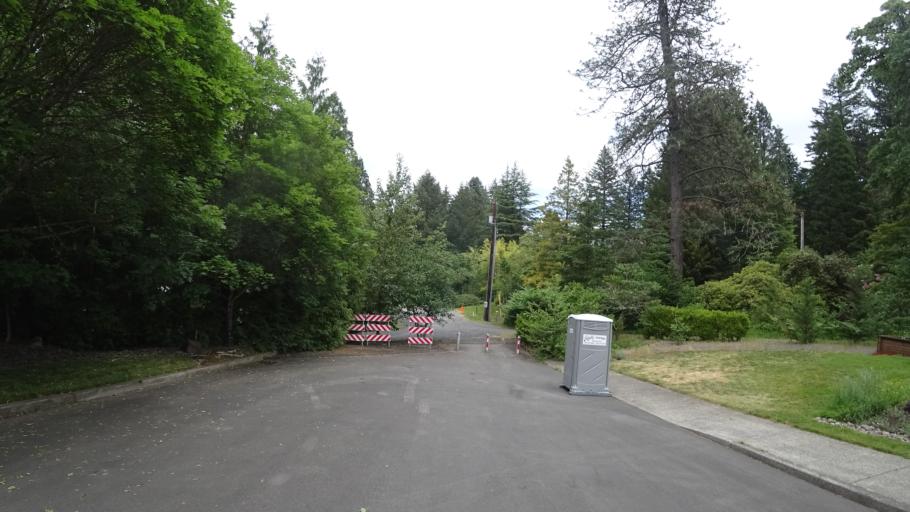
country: US
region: Oregon
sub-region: Clackamas County
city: Lake Oswego
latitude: 45.4445
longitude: -122.7028
